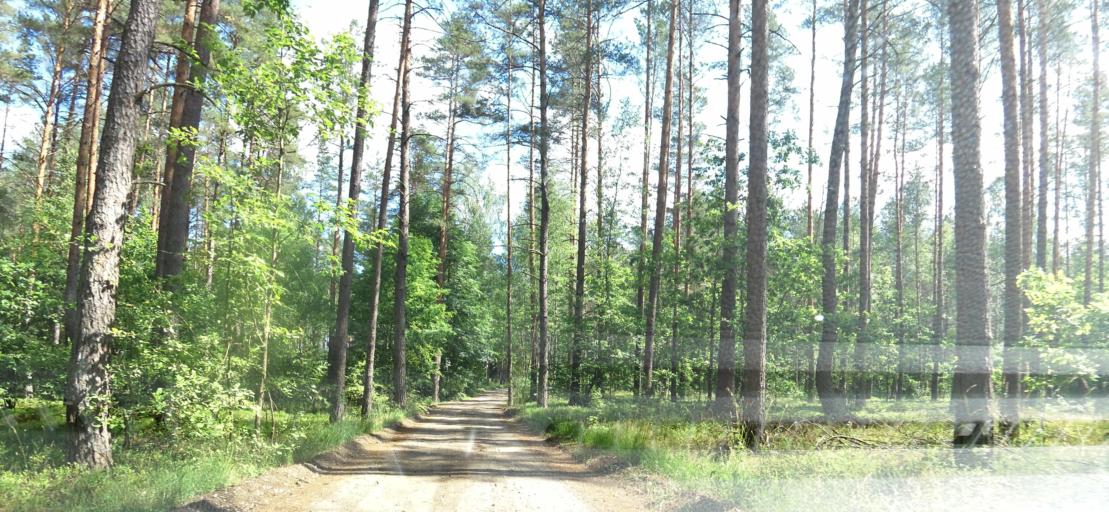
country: LT
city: Nemencine
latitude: 54.8178
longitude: 25.3899
